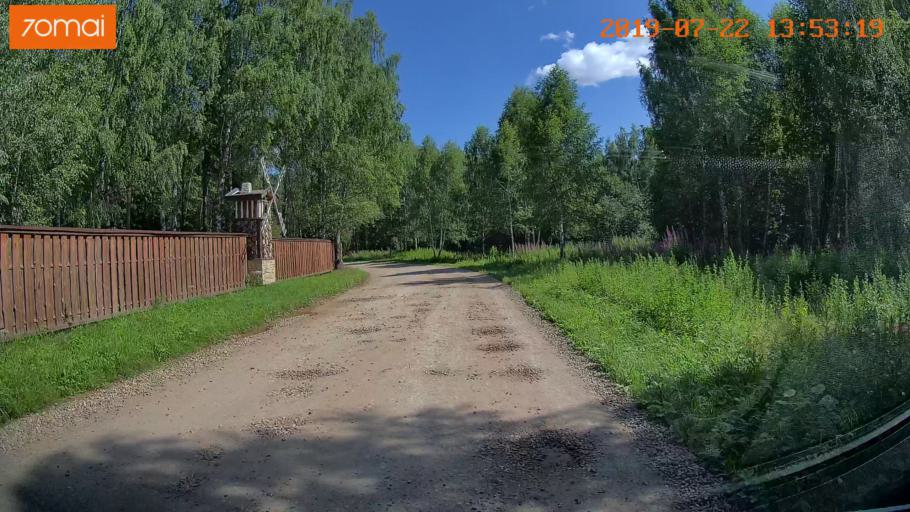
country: RU
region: Ivanovo
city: Novo-Talitsy
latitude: 57.0807
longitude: 40.8761
